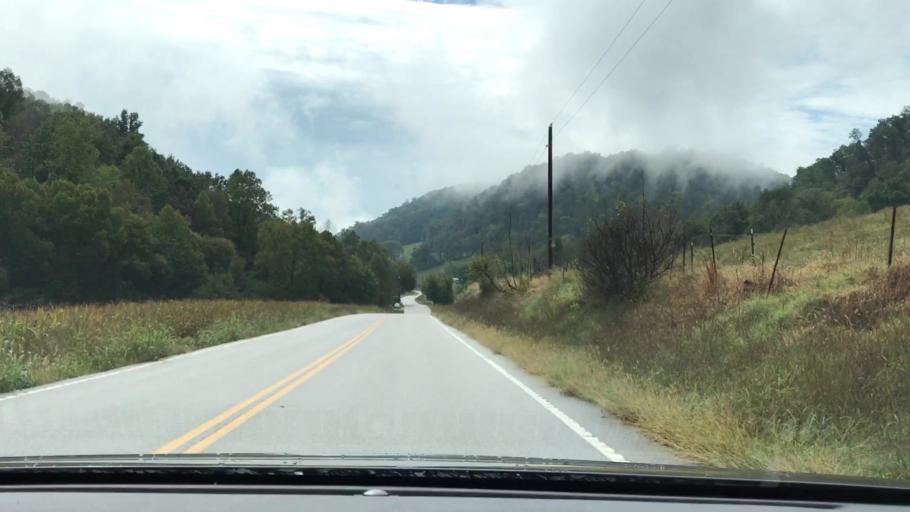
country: US
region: Tennessee
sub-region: Macon County
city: Lafayette
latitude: 36.4019
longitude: -85.9431
